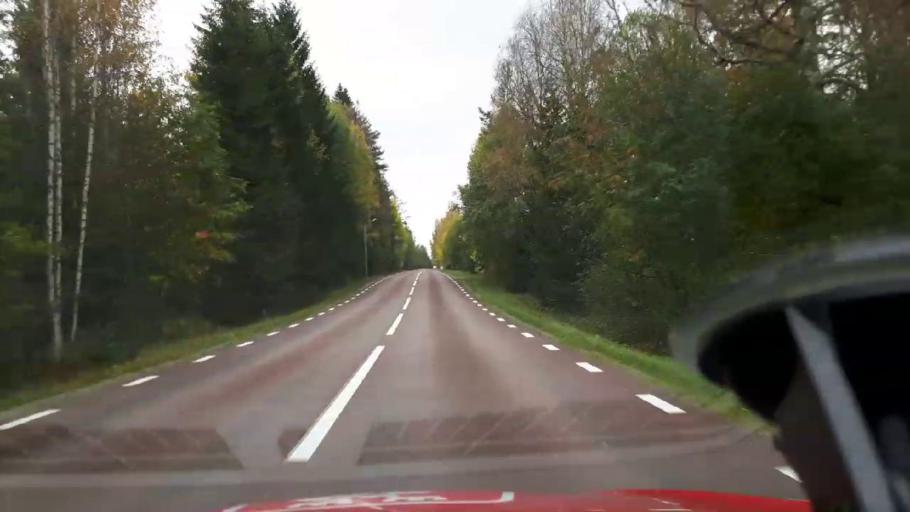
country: SE
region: Jaemtland
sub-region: Harjedalens Kommun
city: Sveg
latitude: 62.1993
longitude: 14.8542
